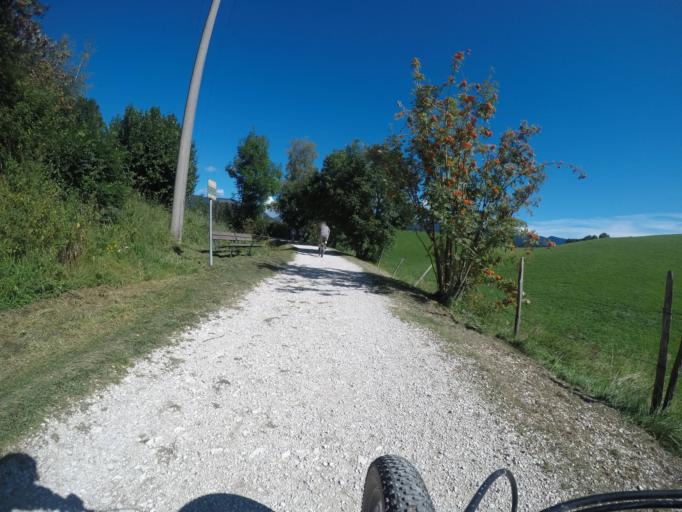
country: IT
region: Veneto
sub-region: Provincia di Vicenza
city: Canove di Roana
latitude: 45.8598
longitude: 11.4766
